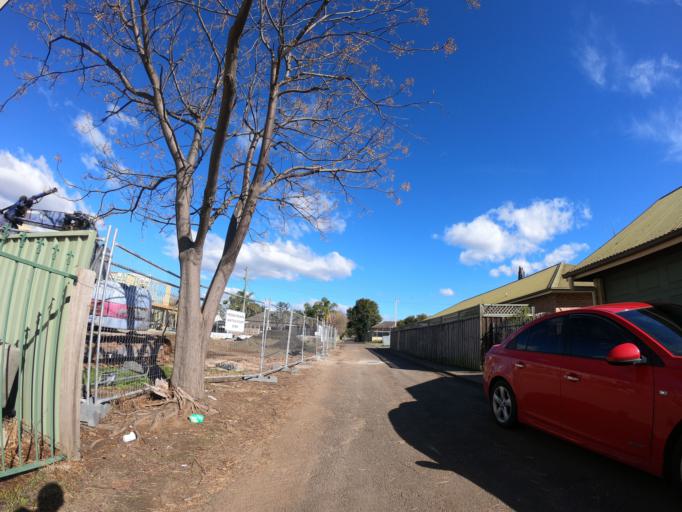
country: AU
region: New South Wales
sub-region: Hawkesbury
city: South Windsor
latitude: -33.6168
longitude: 150.8092
